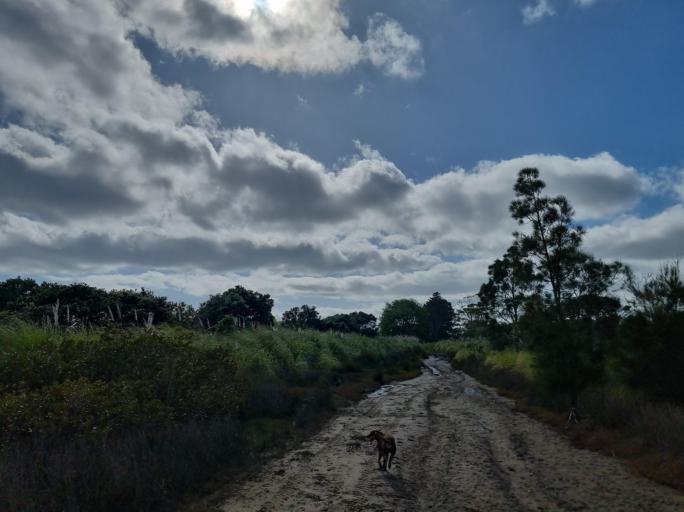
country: NZ
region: Auckland
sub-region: Auckland
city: Wellsford
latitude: -36.1250
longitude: 174.5851
